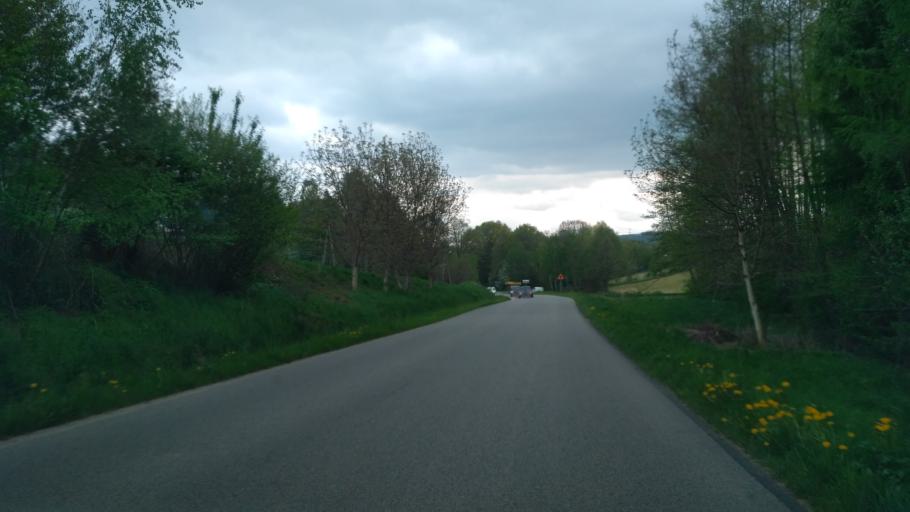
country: PL
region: Subcarpathian Voivodeship
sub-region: Powiat debicki
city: Leki Gorne
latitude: 49.9796
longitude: 21.1580
